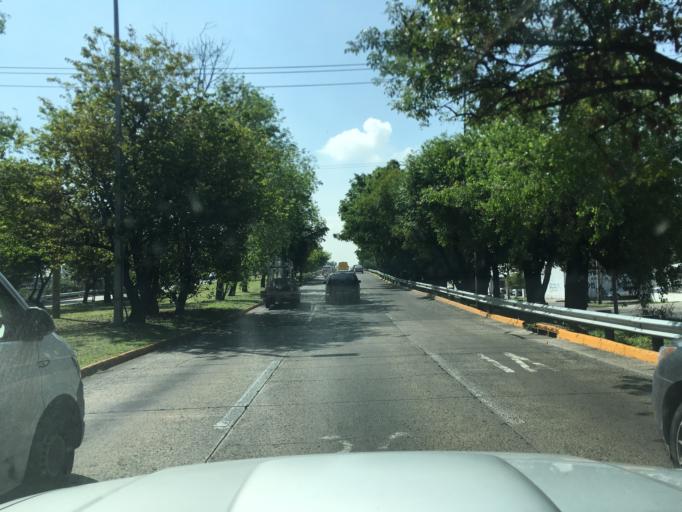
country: MX
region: Jalisco
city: Guadalajara
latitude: 20.6540
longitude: -103.3740
